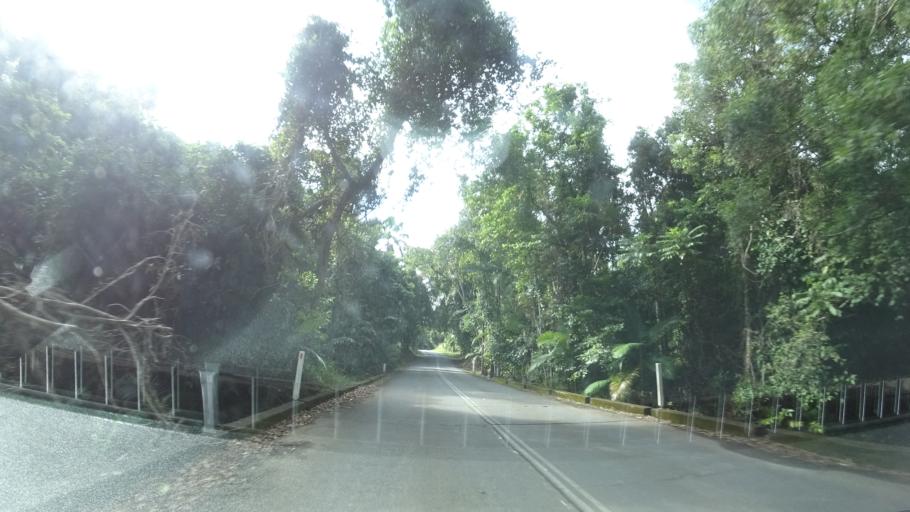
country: AU
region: Queensland
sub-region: Cairns
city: Port Douglas
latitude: -16.1017
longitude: 145.4584
